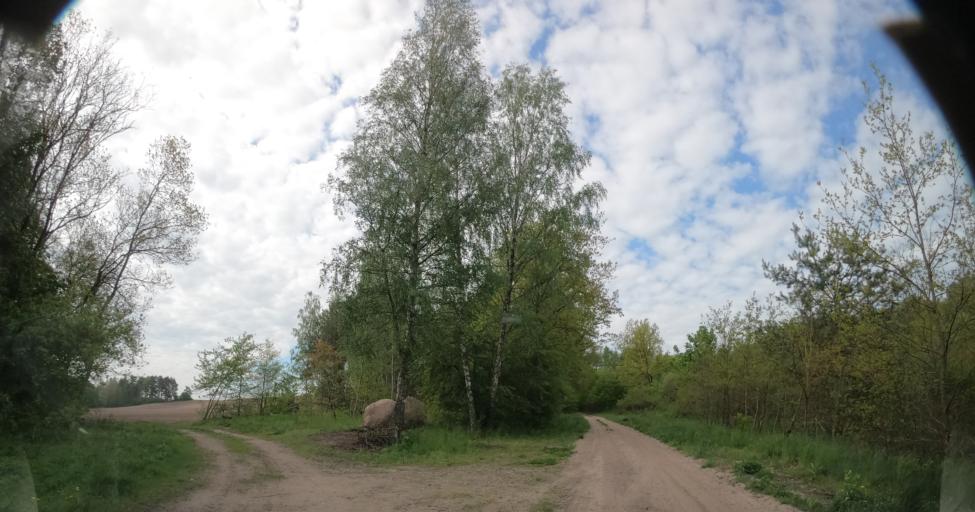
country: PL
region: West Pomeranian Voivodeship
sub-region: Powiat stargardzki
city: Suchan
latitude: 53.2660
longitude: 15.3483
